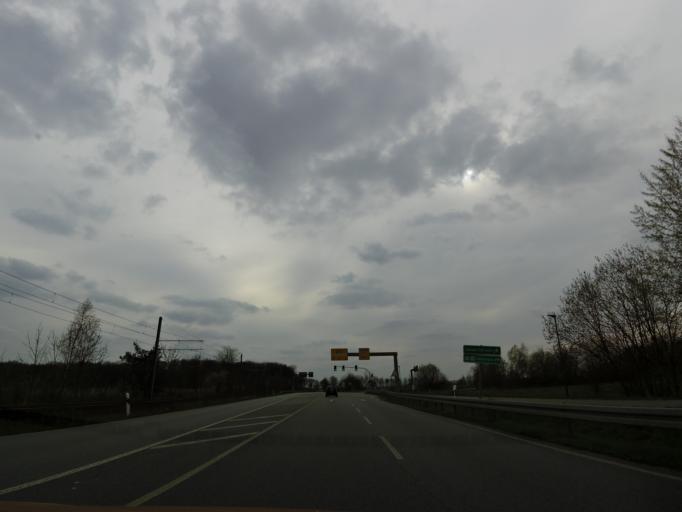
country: DE
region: Brandenburg
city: Frankfurt (Oder)
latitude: 52.3083
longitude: 14.4865
